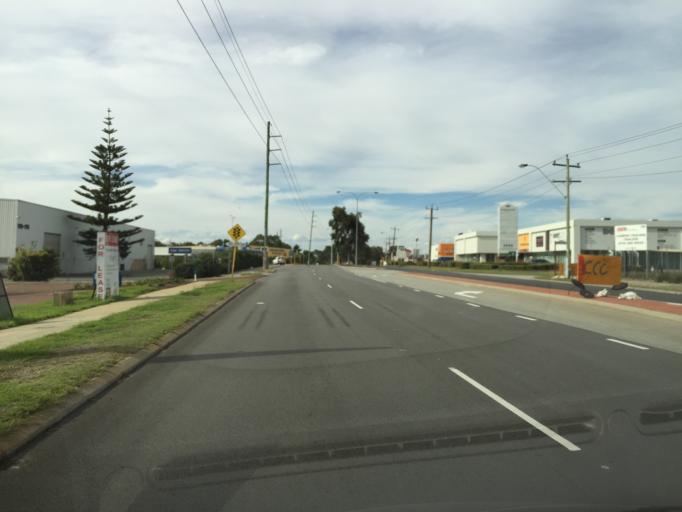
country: AU
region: Western Australia
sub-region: Canning
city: Canning Vale
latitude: -32.0612
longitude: 115.9057
